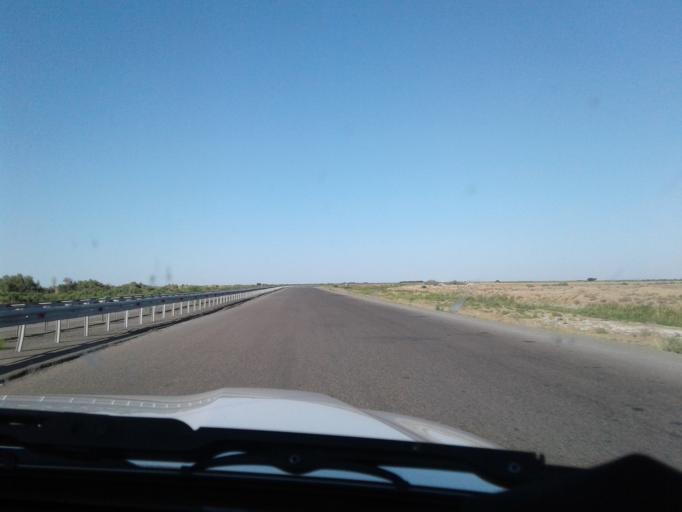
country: TM
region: Ahal
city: Tejen
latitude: 37.3546
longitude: 60.6304
